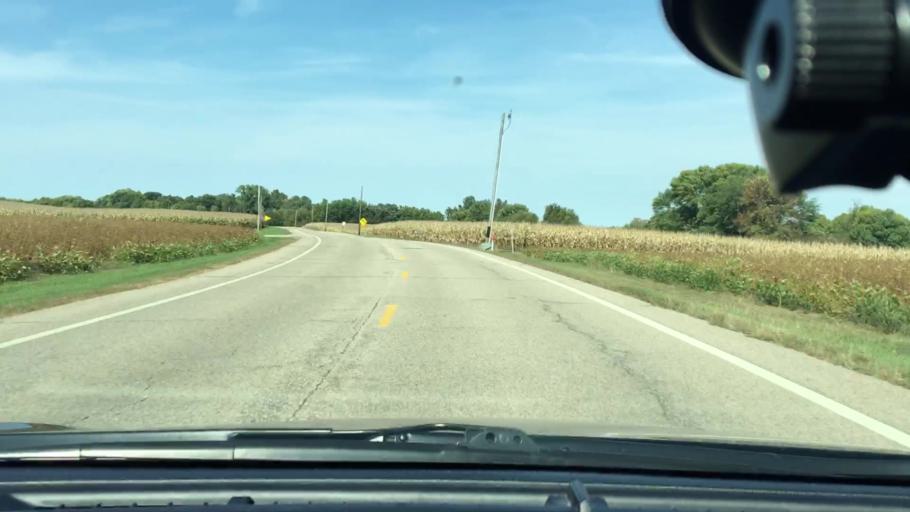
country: US
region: Minnesota
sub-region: Hennepin County
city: Corcoran
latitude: 45.1089
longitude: -93.5655
